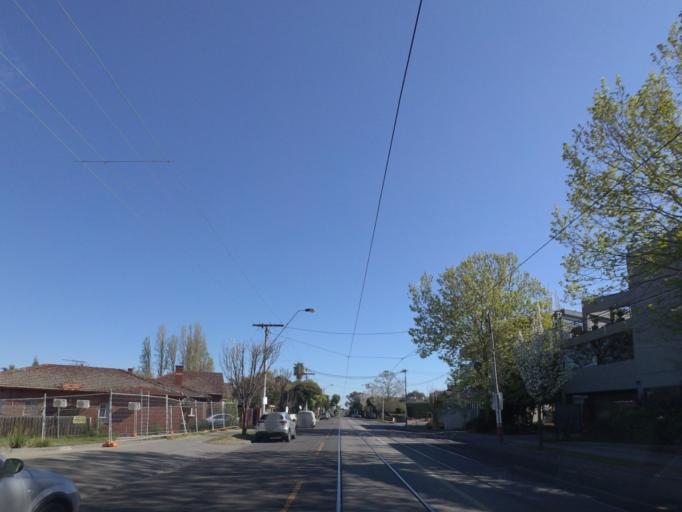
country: AU
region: Victoria
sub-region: Boroondara
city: Kew
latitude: -37.8084
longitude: 145.0280
